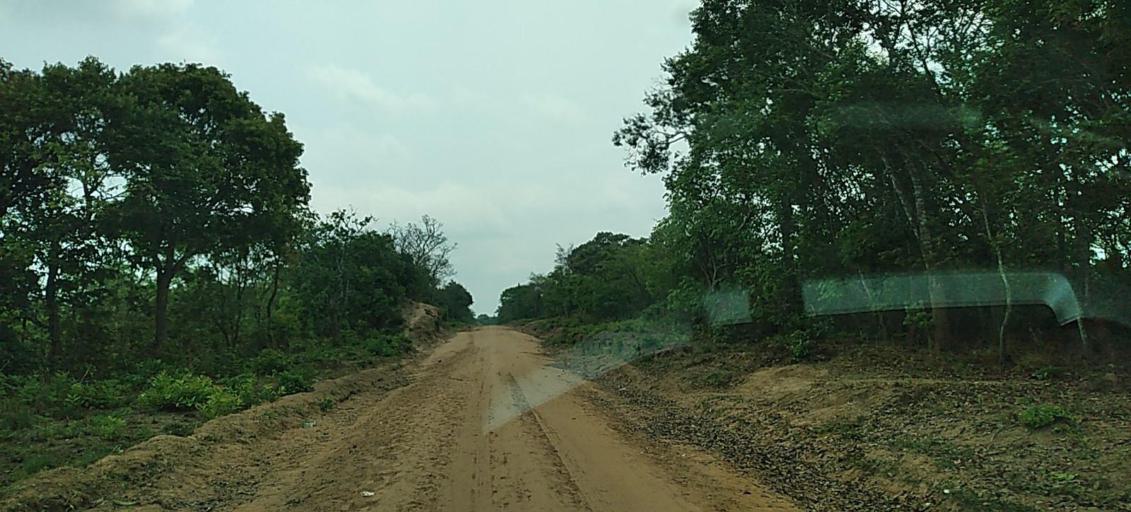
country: ZM
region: North-Western
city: Mwinilunga
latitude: -11.4516
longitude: 24.7531
